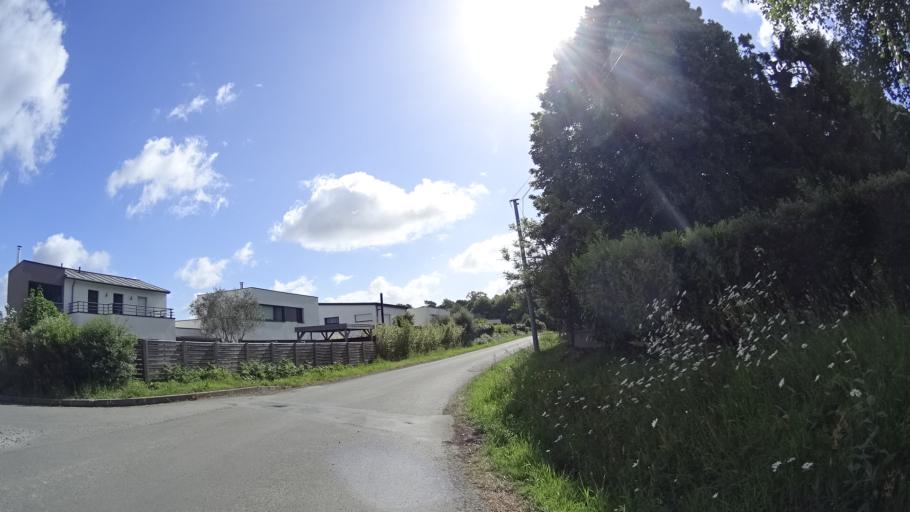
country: FR
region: Brittany
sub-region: Departement d'Ille-et-Vilaine
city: La Chapelle-des-Fougeretz
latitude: 48.1951
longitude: -1.7190
